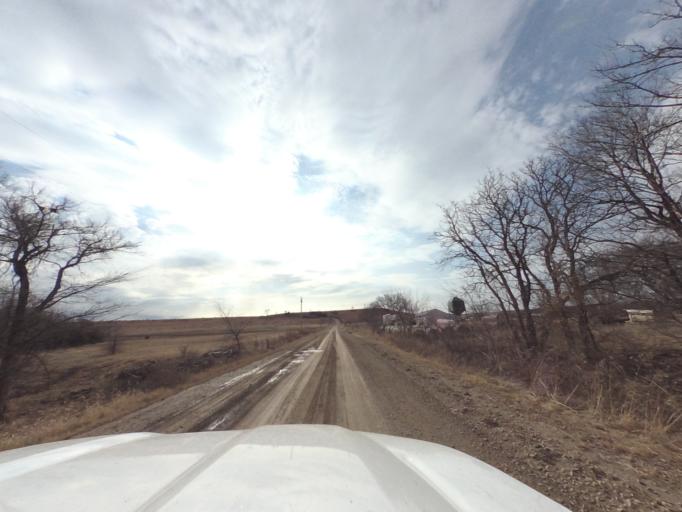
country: US
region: Kansas
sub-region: Chase County
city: Cottonwood Falls
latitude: 38.2877
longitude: -96.7321
